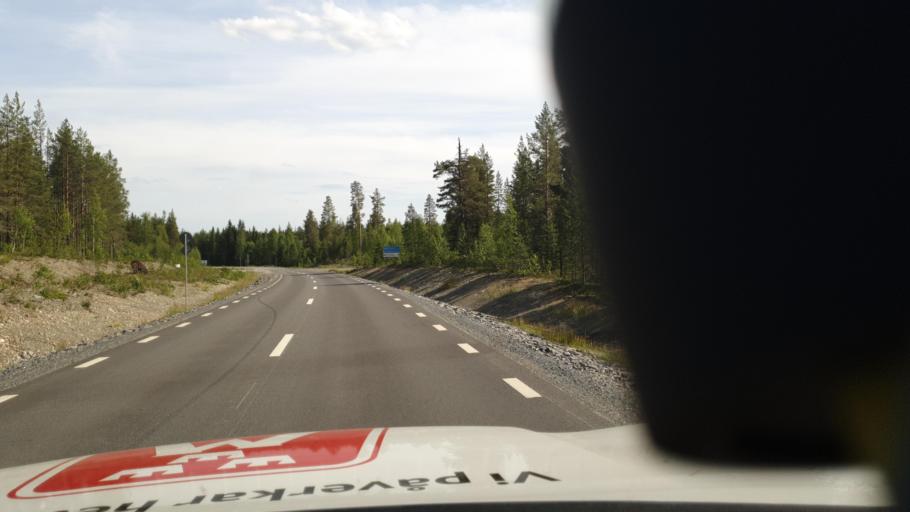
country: SE
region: Vaesterbotten
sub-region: Skelleftea Kommun
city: Langsele
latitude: 64.7552
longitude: 20.3396
